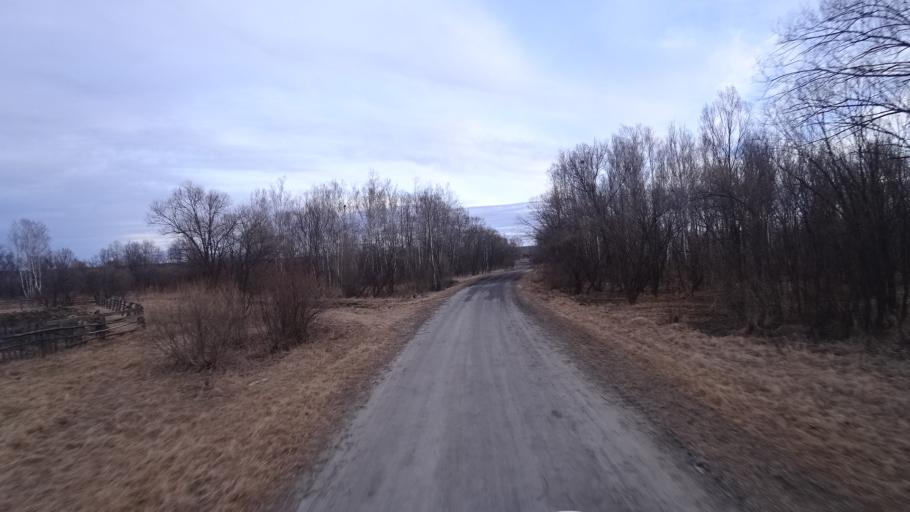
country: RU
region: Amur
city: Bureya
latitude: 50.0200
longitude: 129.7794
